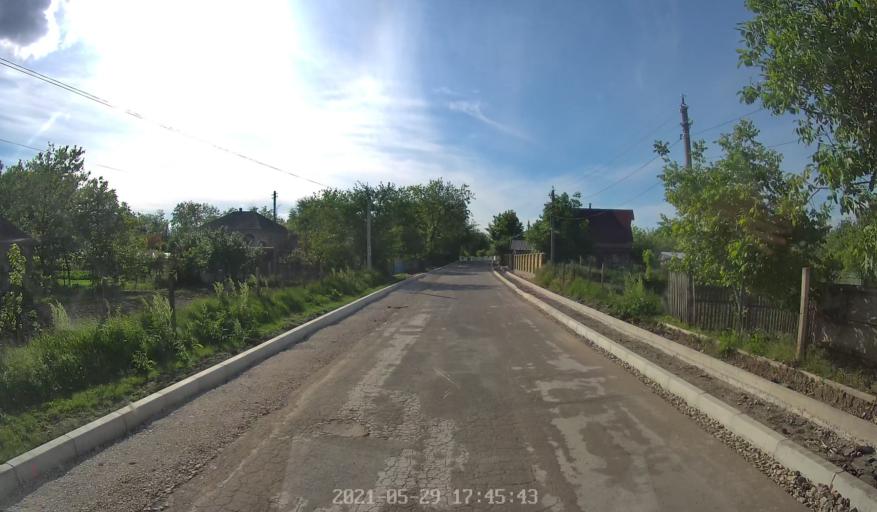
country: MD
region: Laloveni
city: Ialoveni
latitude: 46.8375
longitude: 28.8442
